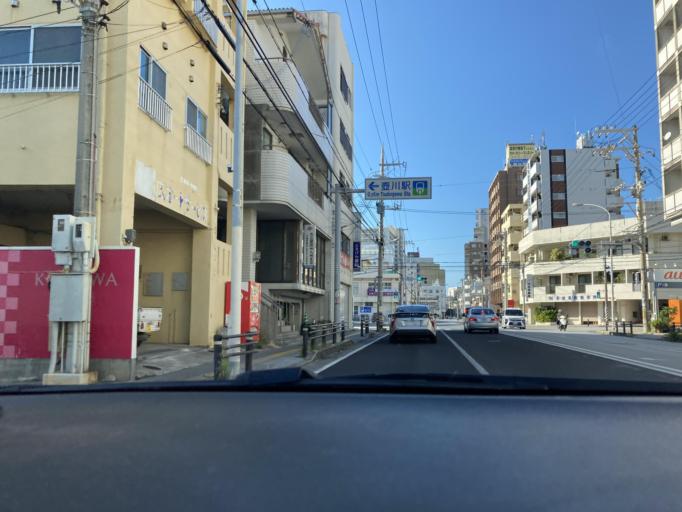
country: JP
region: Okinawa
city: Naha-shi
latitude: 26.2067
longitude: 127.6800
